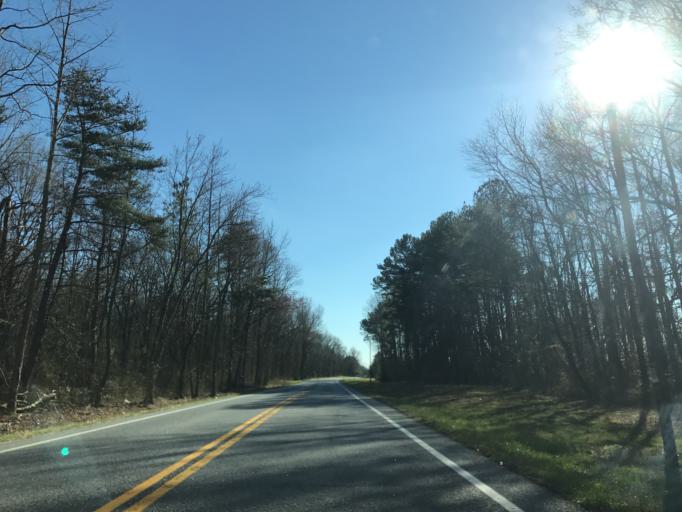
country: US
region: Maryland
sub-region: Caroline County
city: Greensboro
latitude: 39.0459
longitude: -75.8644
